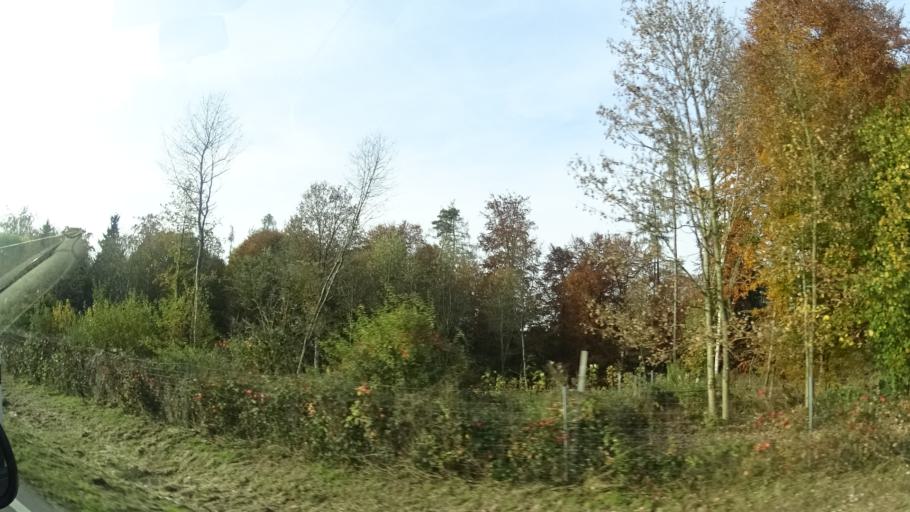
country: DE
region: Baden-Wuerttemberg
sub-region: Karlsruhe Region
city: Aglasterhausen
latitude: 49.3536
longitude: 9.0207
